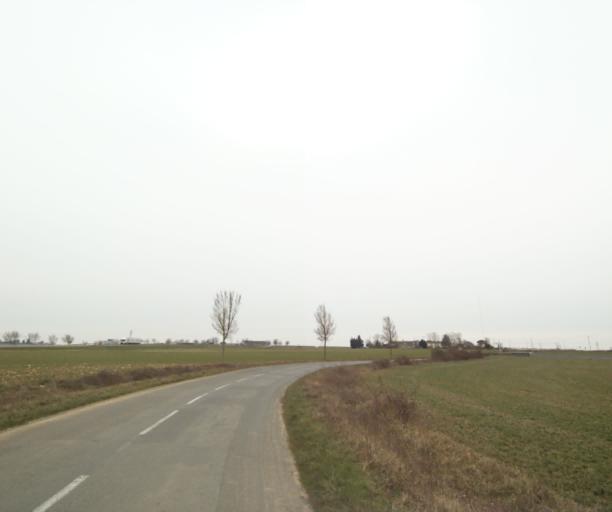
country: FR
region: Poitou-Charentes
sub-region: Departement des Deux-Sevres
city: Bessines
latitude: 46.3454
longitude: -0.5111
